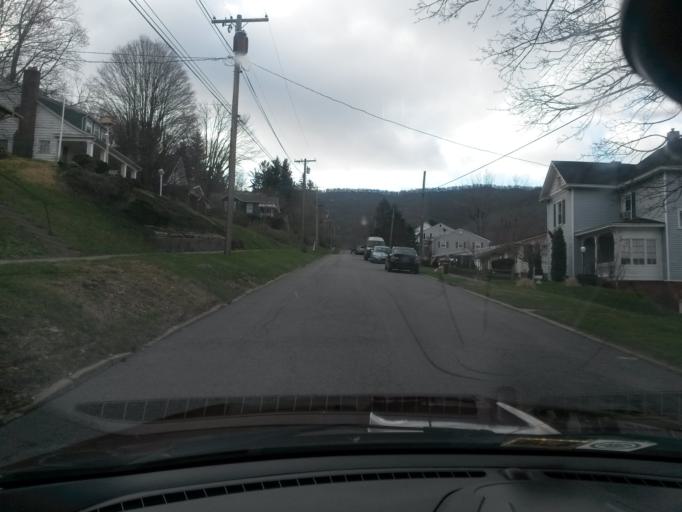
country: US
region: West Virginia
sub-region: Mercer County
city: Bluefield
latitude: 37.2537
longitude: -81.2178
